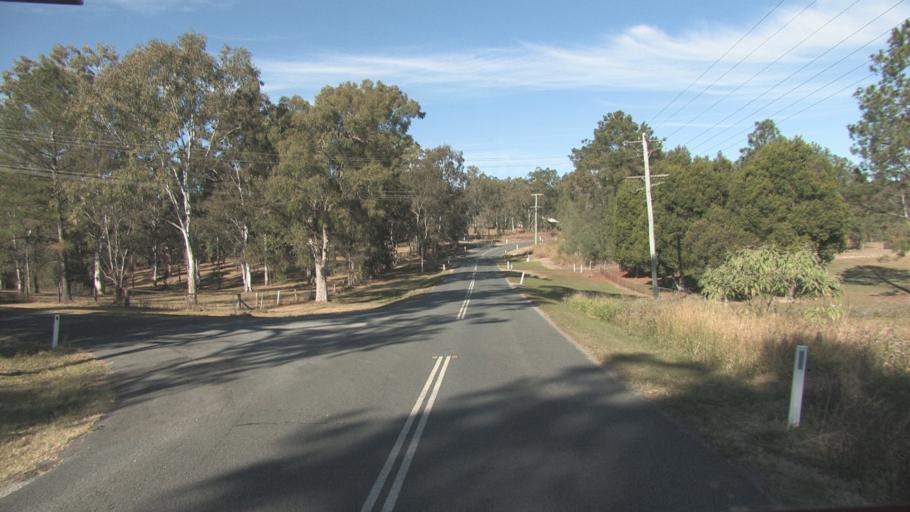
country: AU
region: Queensland
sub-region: Logan
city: Windaroo
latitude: -27.8111
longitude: 153.1705
